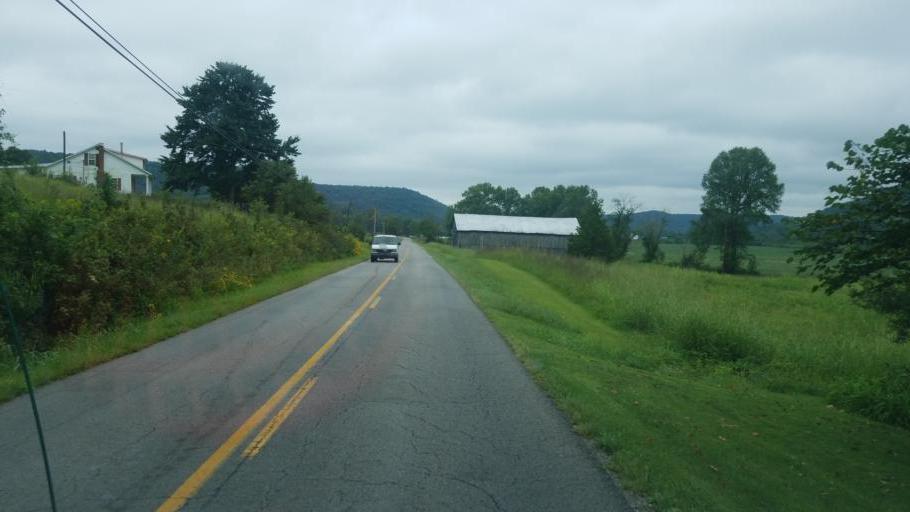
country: US
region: Kentucky
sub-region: Rowan County
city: Morehead
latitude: 38.3267
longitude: -83.5467
